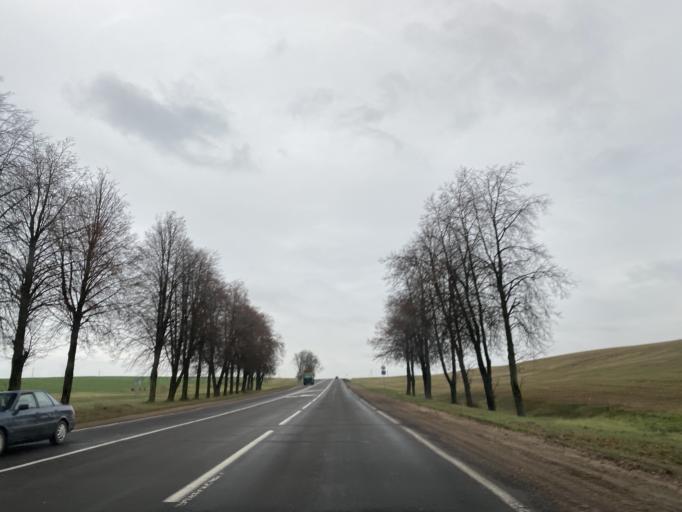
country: BY
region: Minsk
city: Horad Smalyavichy
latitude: 54.0478
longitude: 28.0724
